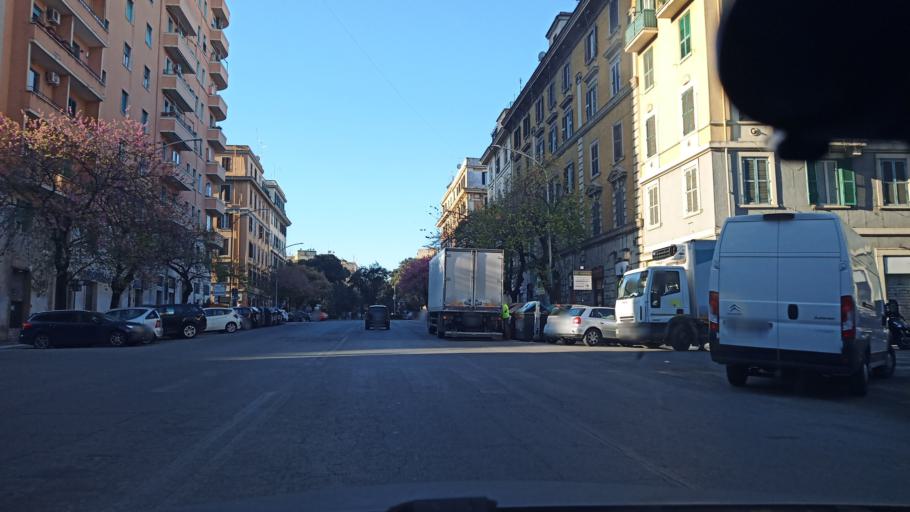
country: IT
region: Latium
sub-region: Citta metropolitana di Roma Capitale
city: Rome
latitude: 41.8836
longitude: 12.5147
